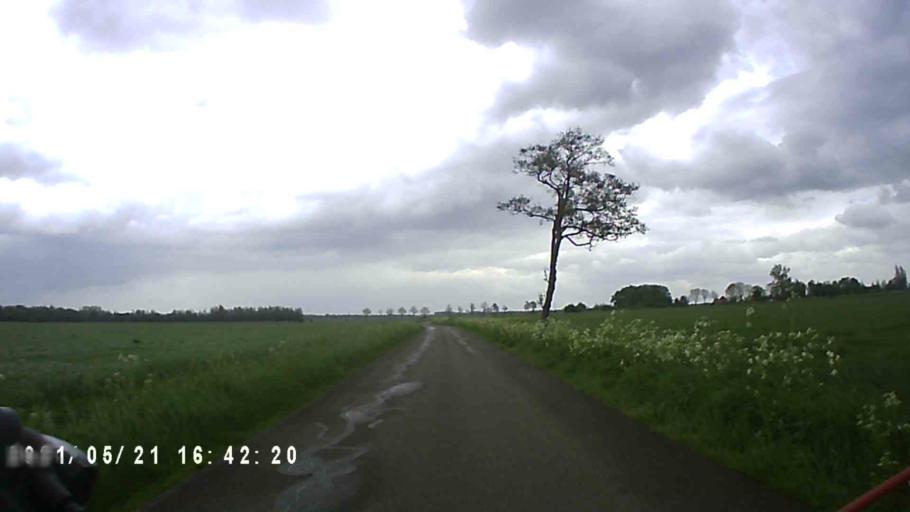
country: NL
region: Groningen
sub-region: Gemeente Zuidhorn
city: Aduard
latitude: 53.1950
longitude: 6.4552
